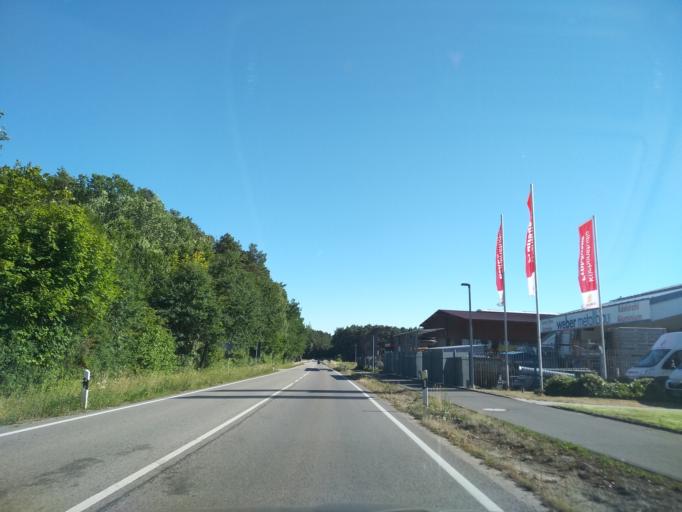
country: DE
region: Bavaria
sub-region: Regierungsbezirk Mittelfranken
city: Rottenbach
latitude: 49.6592
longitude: 10.9181
